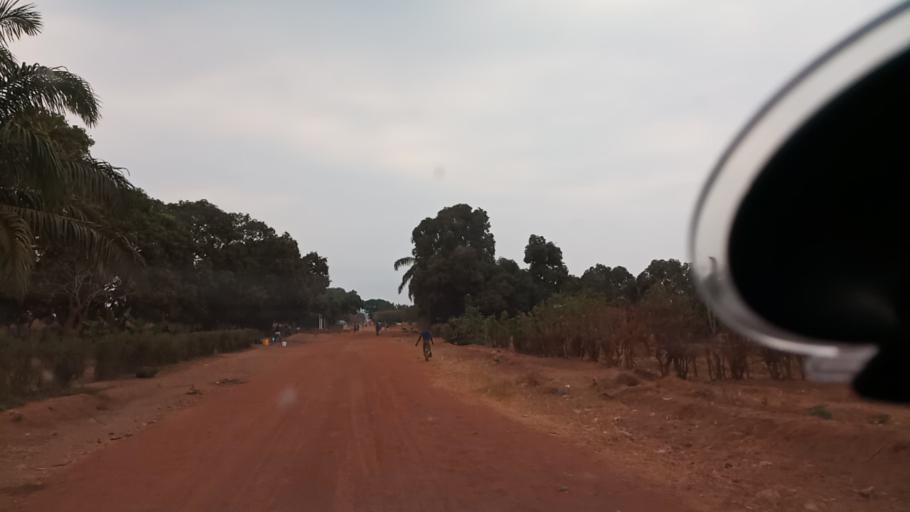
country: ZM
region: Luapula
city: Nchelenge
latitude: -9.2768
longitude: 28.3295
